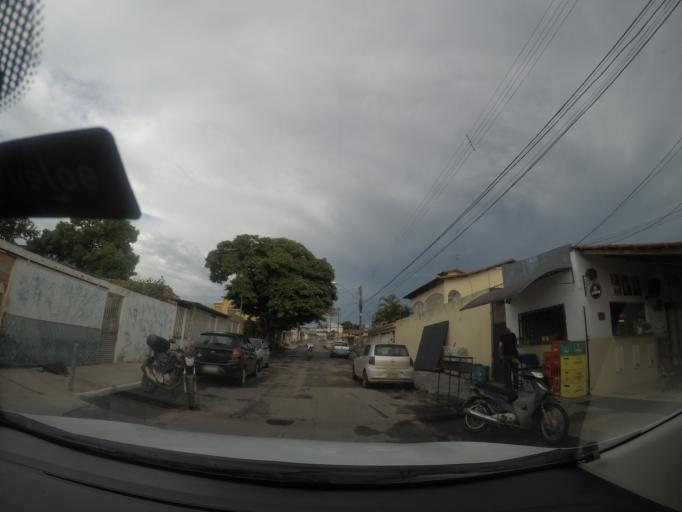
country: BR
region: Goias
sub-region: Goiania
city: Goiania
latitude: -16.6659
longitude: -49.2873
